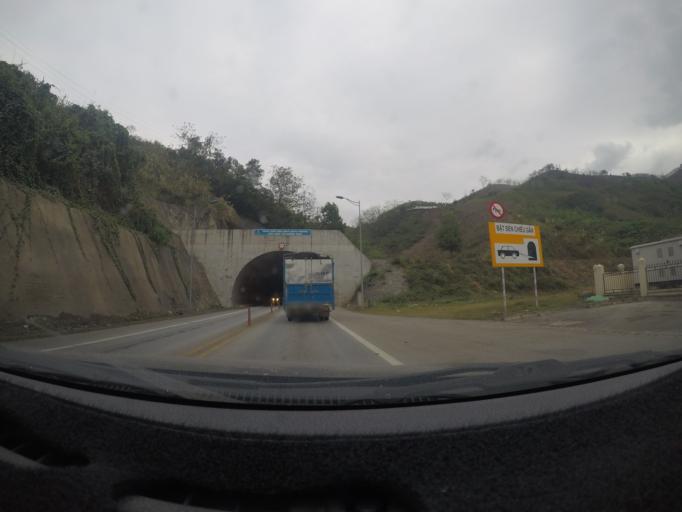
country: VN
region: Lao Cai
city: Thi Tran Pho Rang
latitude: 22.0957
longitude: 104.4271
